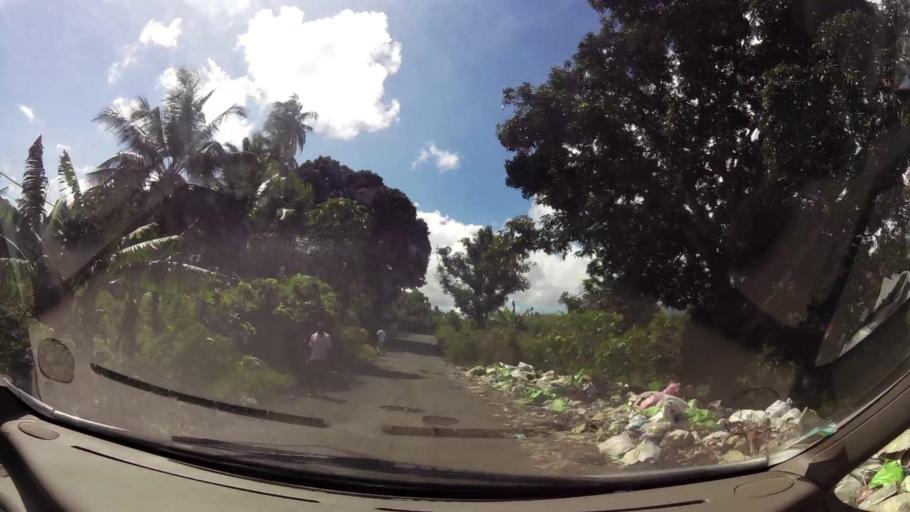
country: KM
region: Grande Comore
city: Mavingouni
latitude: -11.7405
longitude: 43.2459
